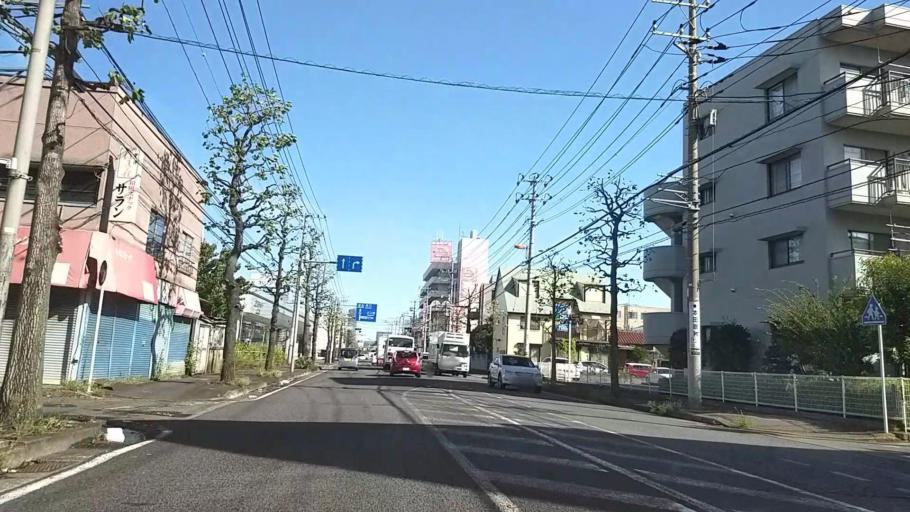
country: JP
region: Kanagawa
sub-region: Kawasaki-shi
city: Kawasaki
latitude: 35.5529
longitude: 139.6593
